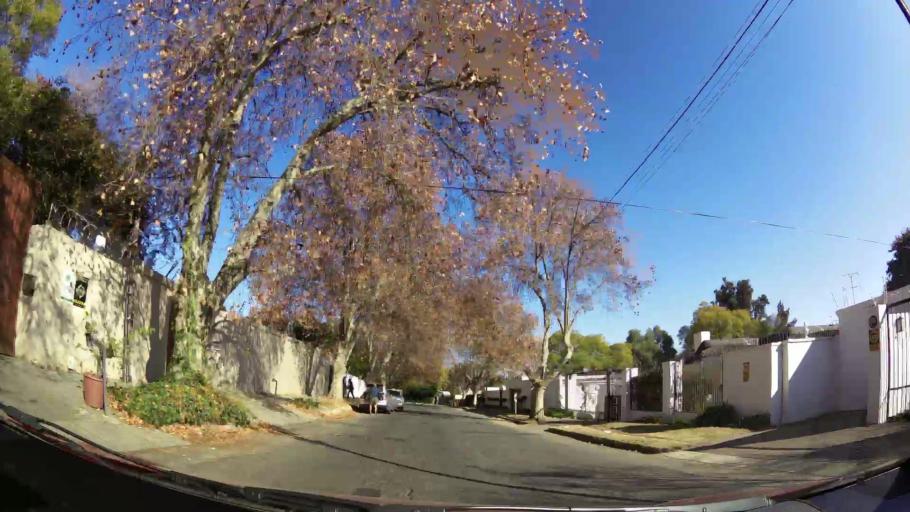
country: ZA
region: Gauteng
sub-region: City of Johannesburg Metropolitan Municipality
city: Johannesburg
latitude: -26.1427
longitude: 28.0329
